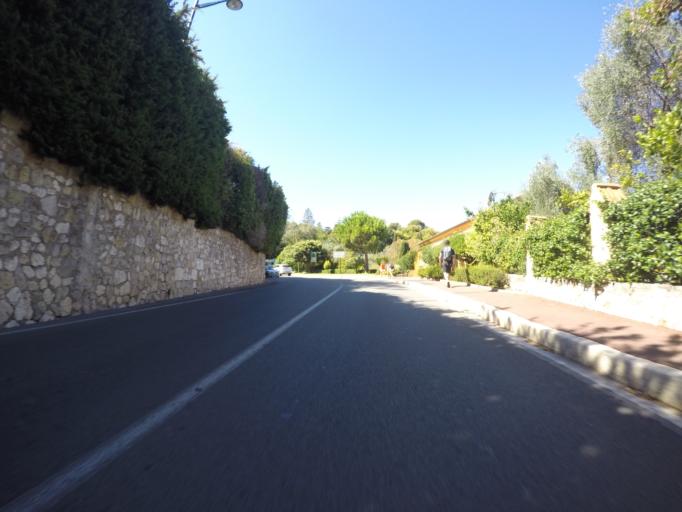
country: FR
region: Provence-Alpes-Cote d'Azur
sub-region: Departement des Alpes-Maritimes
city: Saint-Jean-Cap-Ferrat
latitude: 43.6931
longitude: 7.3287
